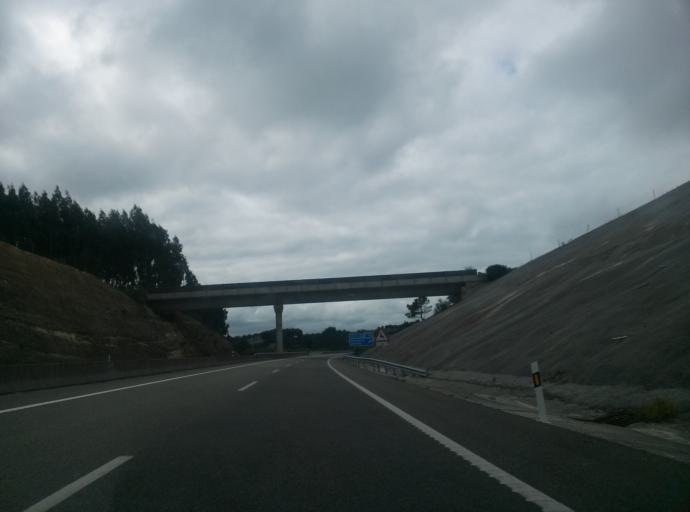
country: ES
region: Galicia
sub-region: Provincia de Lugo
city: Vilalba
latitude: 43.3463
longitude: -7.7293
